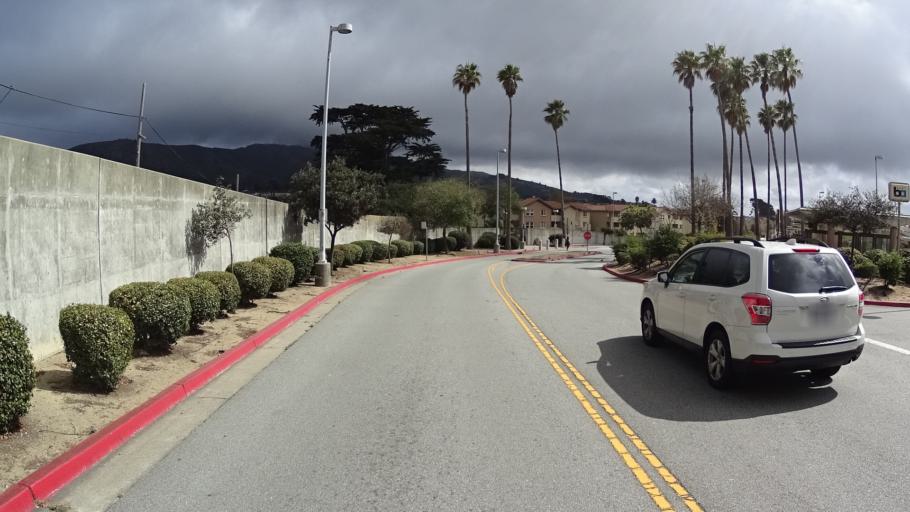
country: US
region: California
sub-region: San Mateo County
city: Colma
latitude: 37.6853
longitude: -122.4663
